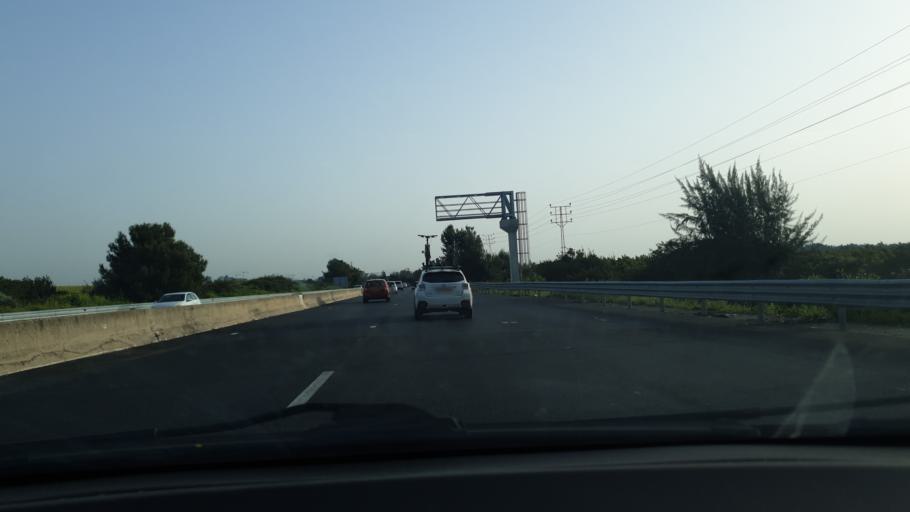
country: IL
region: Central District
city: Tel Mond
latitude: 32.2308
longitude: 34.8839
